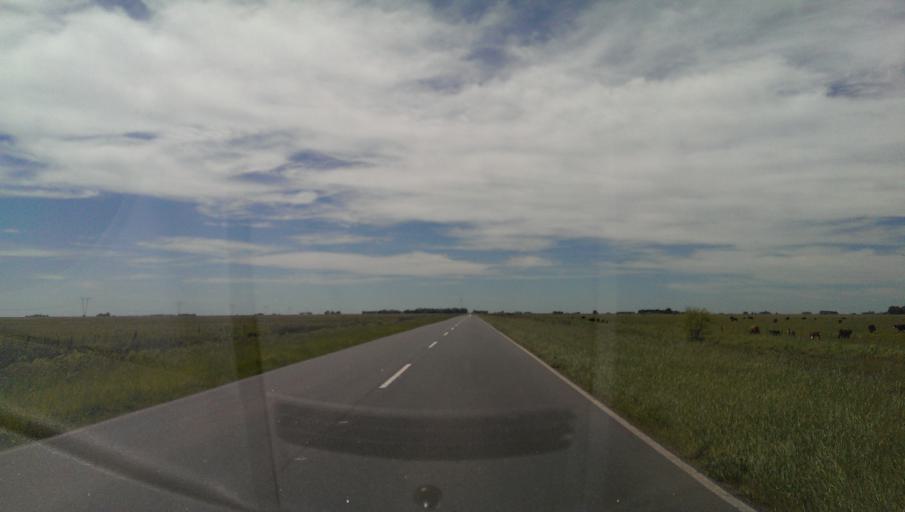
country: AR
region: Buenos Aires
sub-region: Partido de Laprida
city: Laprida
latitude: -37.2125
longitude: -60.6857
